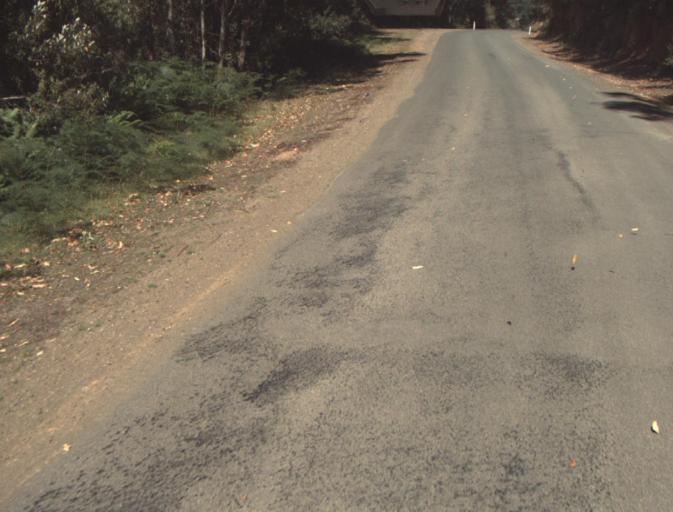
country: AU
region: Tasmania
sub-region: Dorset
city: Scottsdale
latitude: -41.3161
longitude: 147.4043
